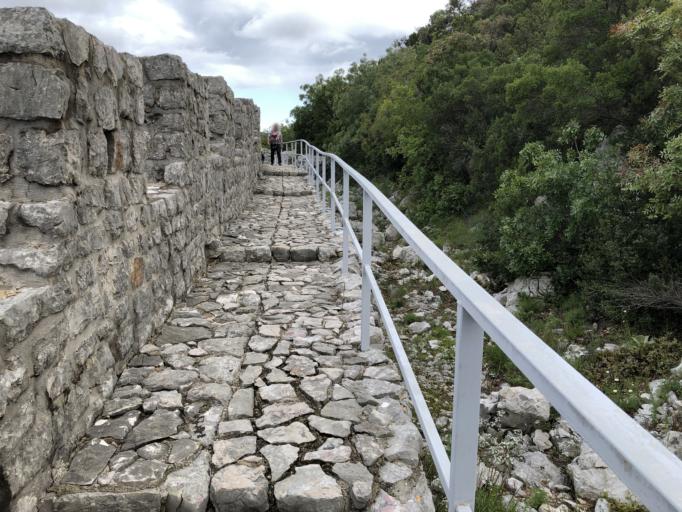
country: HR
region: Dubrovacko-Neretvanska
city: Ston
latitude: 42.8424
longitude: 17.6988
